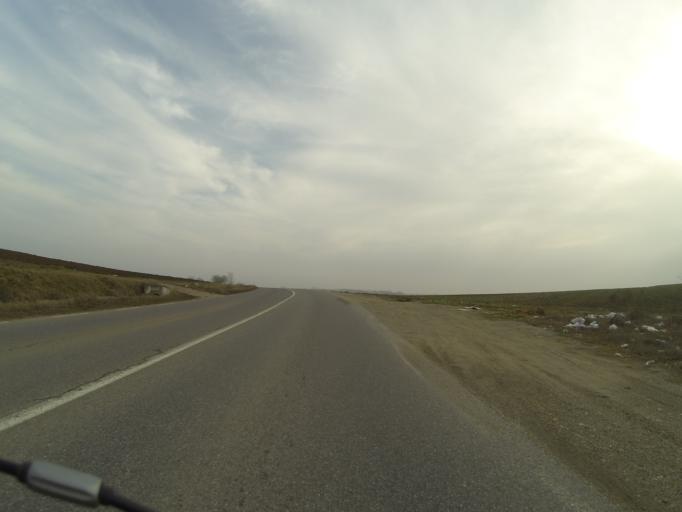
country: RO
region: Mehedinti
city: Vanju-Mare
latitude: 44.4099
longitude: 22.8857
